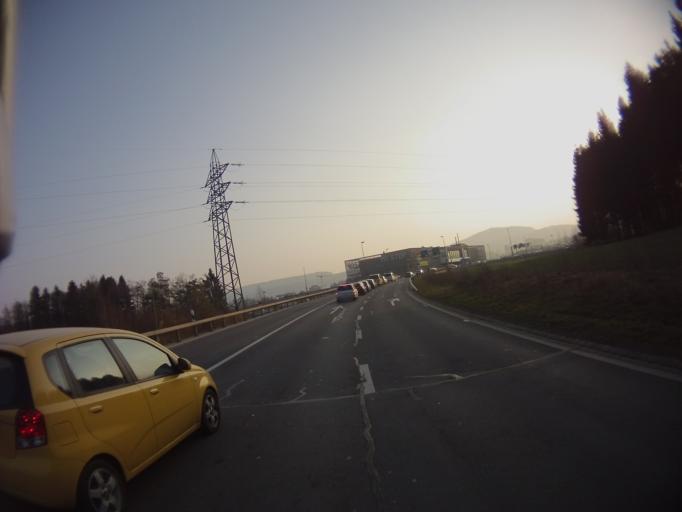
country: CH
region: Zurich
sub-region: Bezirk Affoltern
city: Obfelden / Toussen
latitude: 47.2709
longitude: 8.4356
